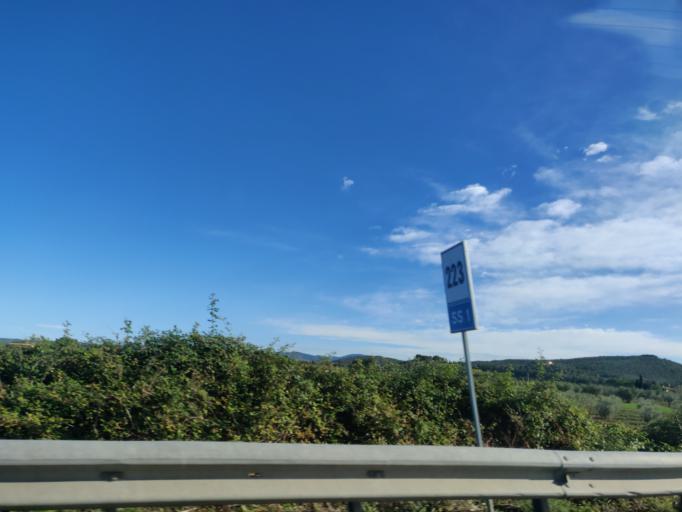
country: IT
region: Tuscany
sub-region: Provincia di Grosseto
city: Scarlino Scalo
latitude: 42.9590
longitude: 10.8186
